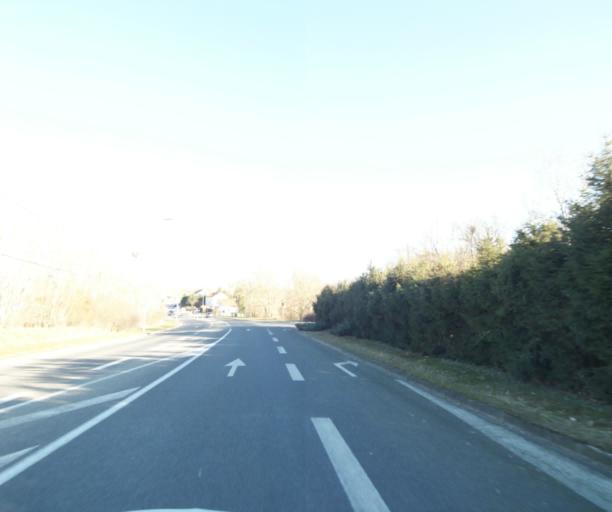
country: FR
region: Lorraine
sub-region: Departement de Meurthe-et-Moselle
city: Saint-Nicolas-de-Port
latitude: 48.6360
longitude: 6.2836
